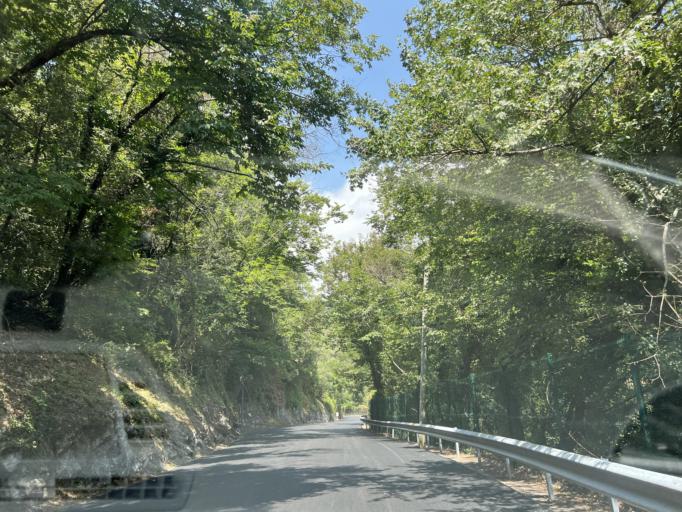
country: FR
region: Provence-Alpes-Cote d'Azur
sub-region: Departement des Alpes-Maritimes
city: Tourrettes-sur-Loup
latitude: 43.7589
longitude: 6.9902
